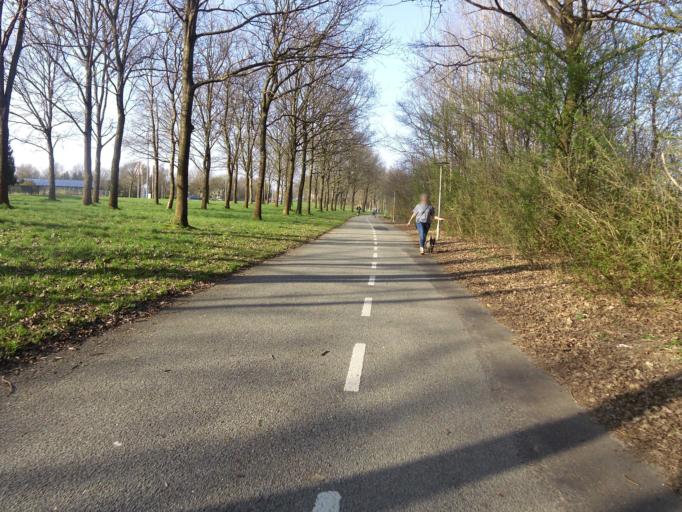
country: DK
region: South Denmark
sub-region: Vejen Kommune
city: Vejen
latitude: 55.4680
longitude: 9.1216
